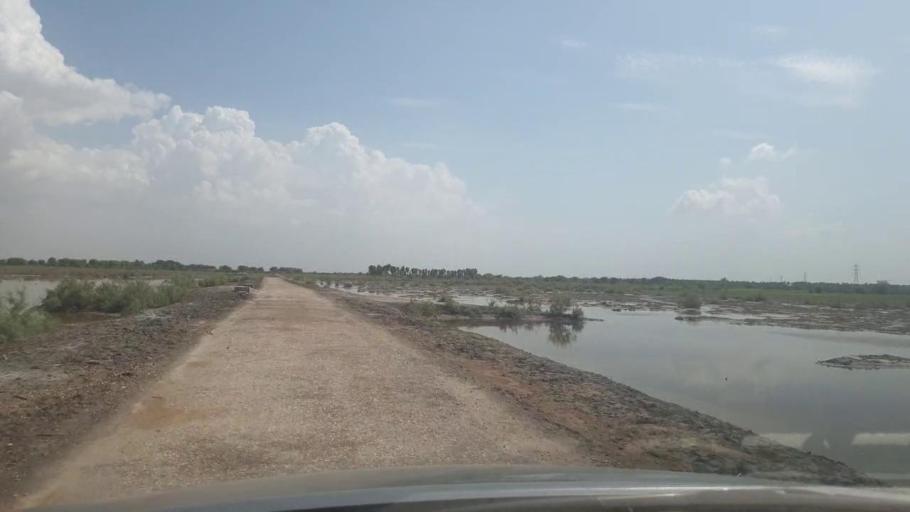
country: PK
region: Sindh
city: Khairpur
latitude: 27.5425
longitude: 68.8038
